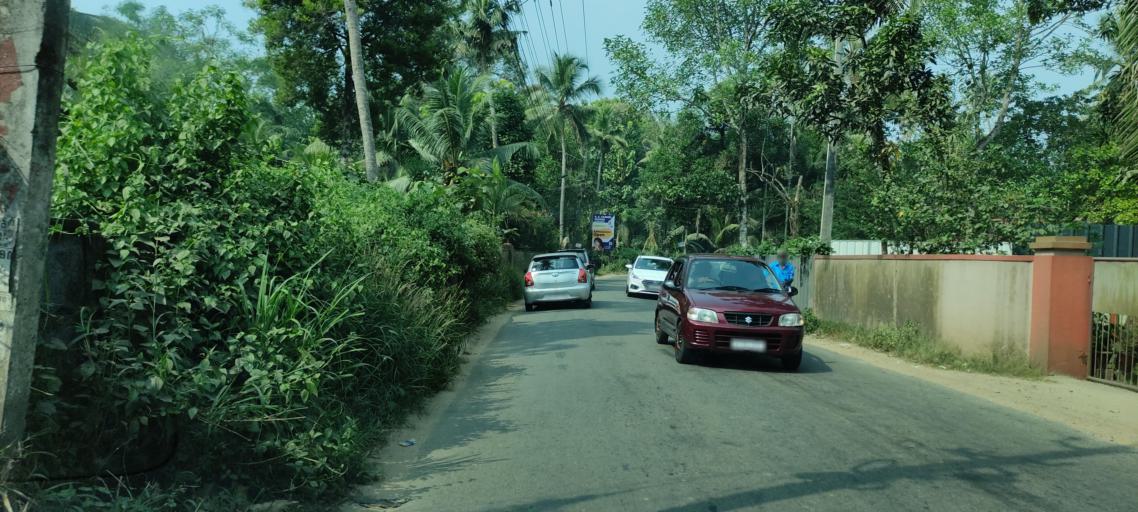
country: IN
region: Kerala
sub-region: Alappuzha
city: Shertallai
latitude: 9.6750
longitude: 76.4212
